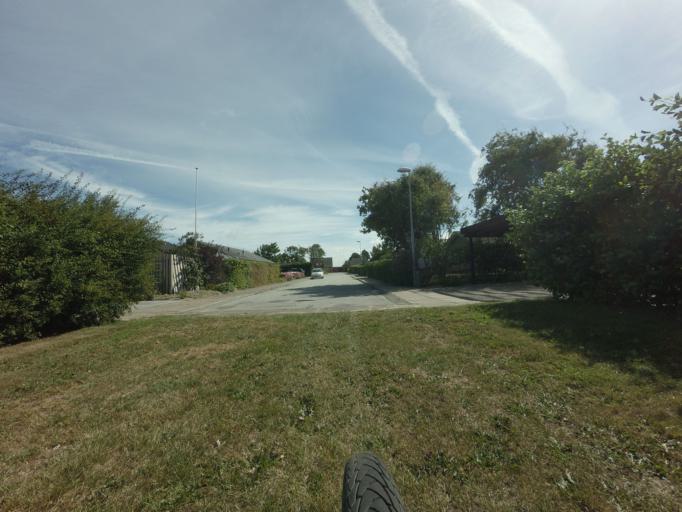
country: DK
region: North Denmark
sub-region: Jammerbugt Kommune
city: Pandrup
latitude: 57.3407
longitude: 9.7737
